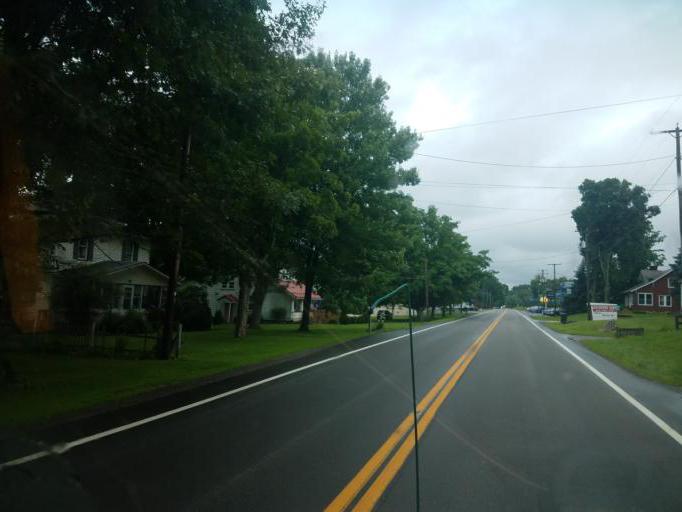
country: US
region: Ohio
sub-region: Carroll County
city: Carrollton
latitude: 40.5621
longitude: -81.0654
